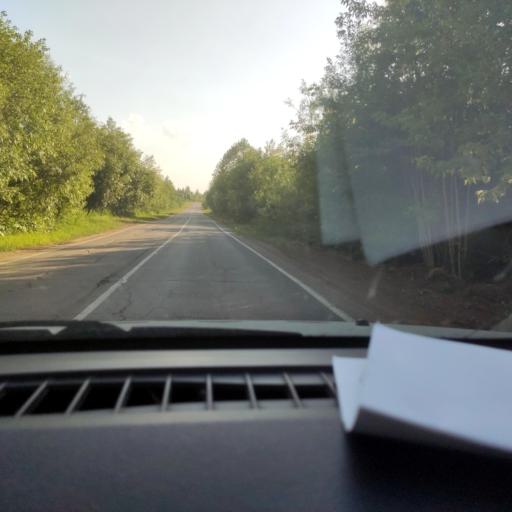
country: RU
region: Perm
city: Krasnokamsk
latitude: 58.1444
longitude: 55.7099
